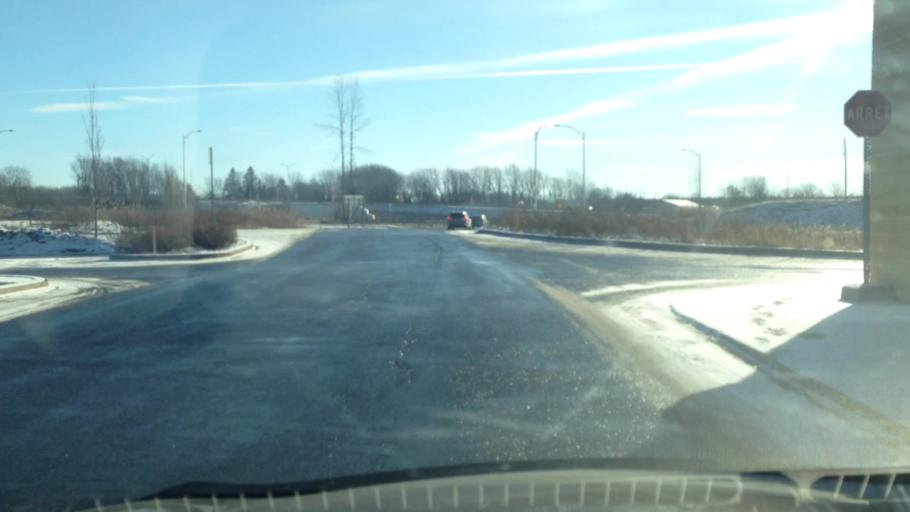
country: CA
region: Quebec
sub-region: Monteregie
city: Mercier
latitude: 45.3428
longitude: -73.7619
